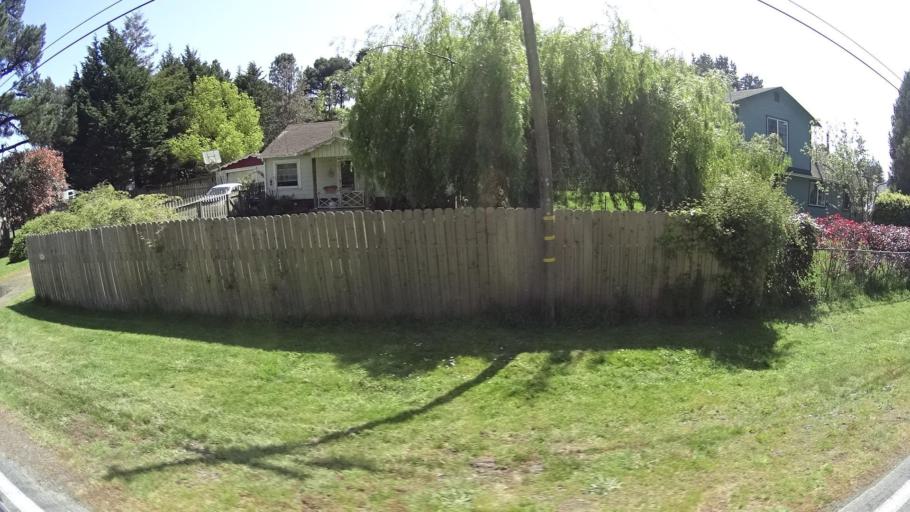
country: US
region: California
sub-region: Humboldt County
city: Hydesville
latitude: 40.5492
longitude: -124.1043
